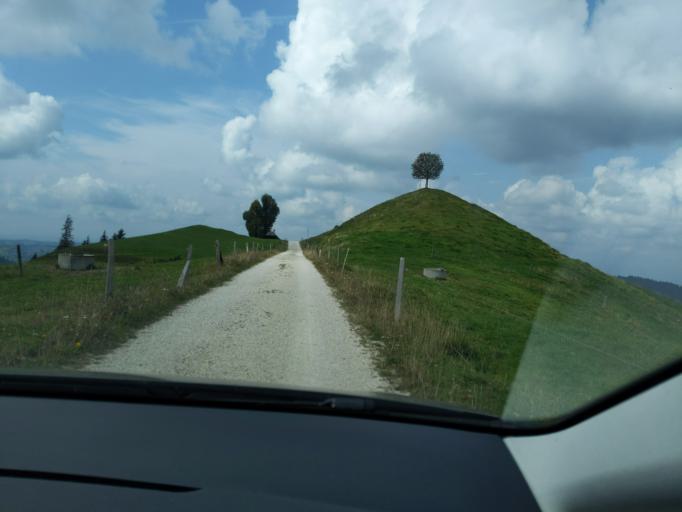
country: CH
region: Bern
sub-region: Oberaargau
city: Wyssachen
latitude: 47.0270
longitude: 7.8314
